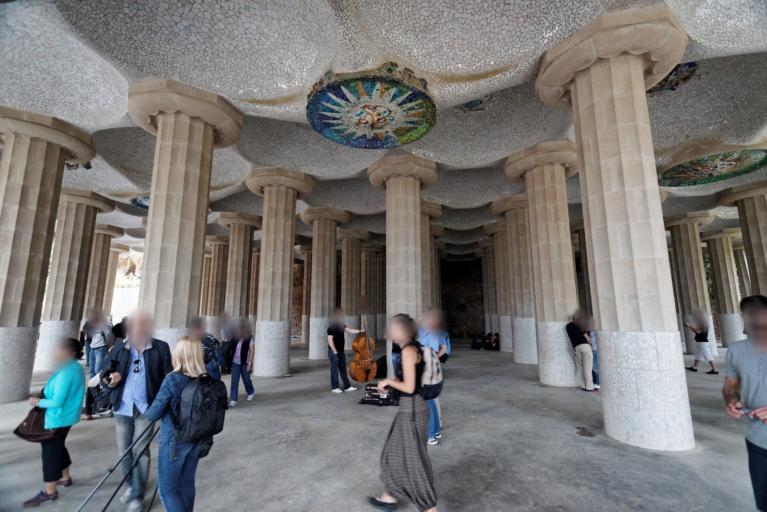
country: ES
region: Catalonia
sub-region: Provincia de Barcelona
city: Gracia
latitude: 41.4137
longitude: 2.1528
